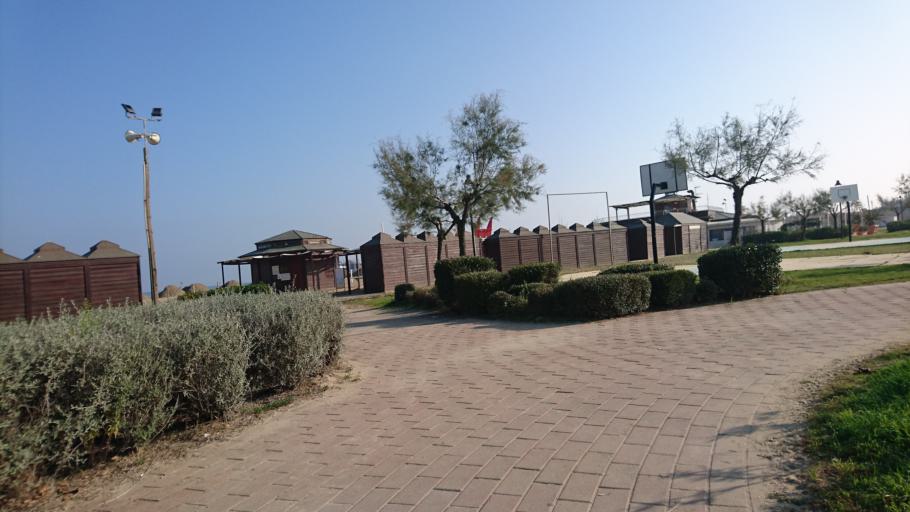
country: IT
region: Emilia-Romagna
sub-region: Provincia di Rimini
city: Rimini
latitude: 44.0751
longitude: 12.5659
